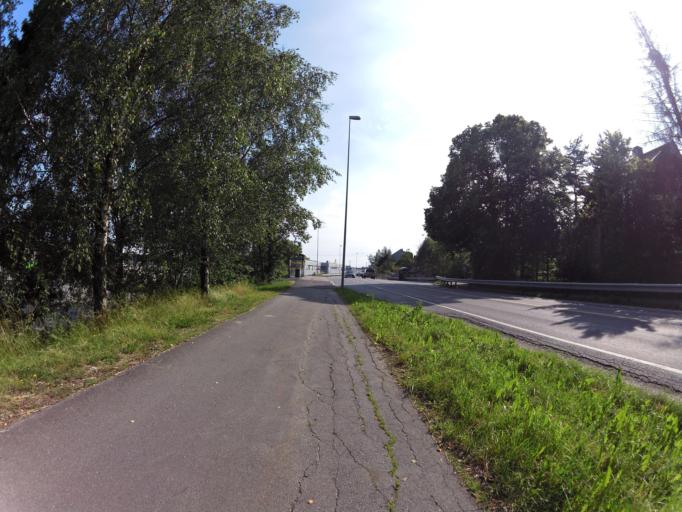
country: NO
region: Ostfold
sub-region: Fredrikstad
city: Fredrikstad
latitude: 59.2504
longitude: 10.9903
